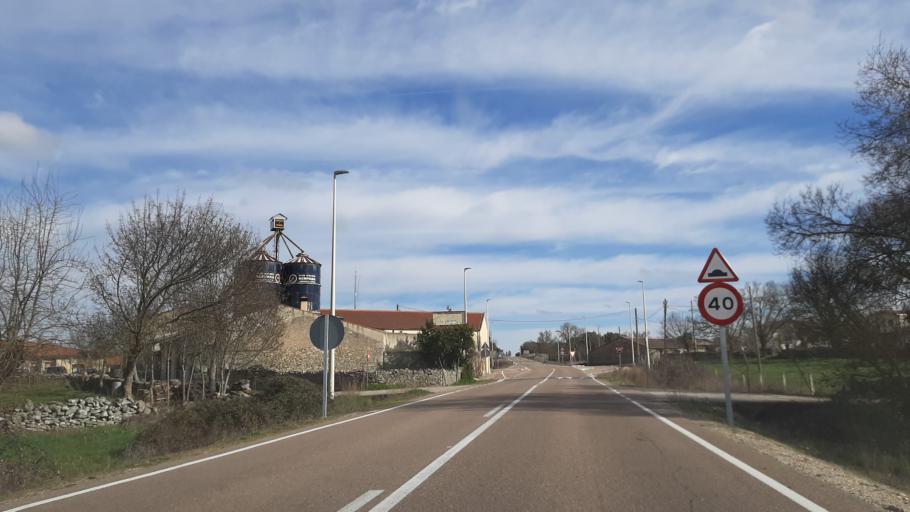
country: ES
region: Castille and Leon
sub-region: Provincia de Salamanca
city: Monleras
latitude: 41.1836
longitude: -6.2272
